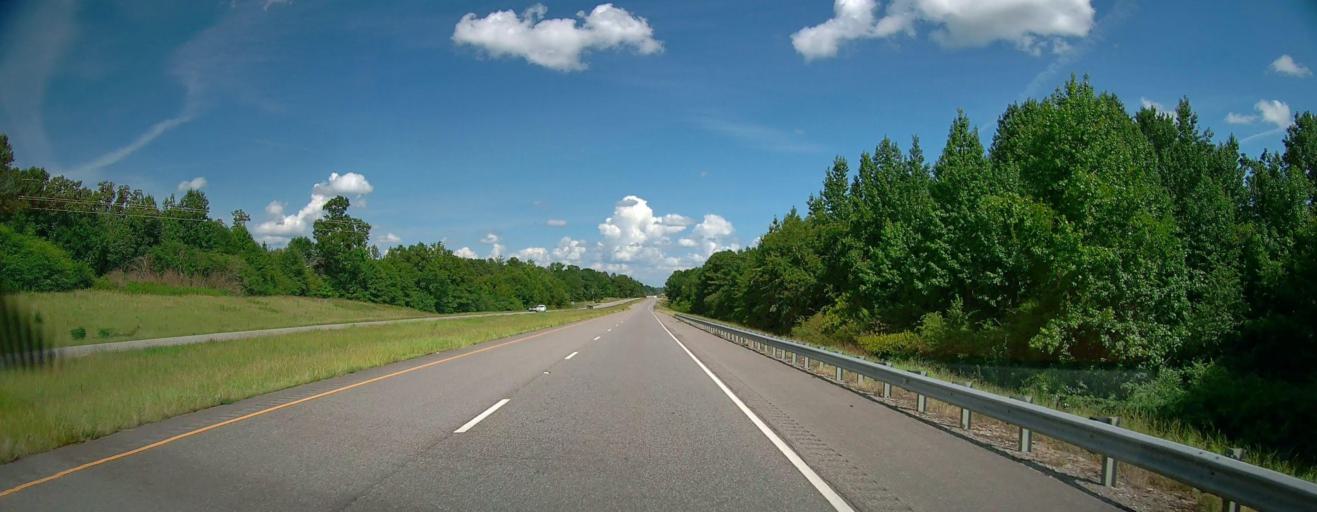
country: US
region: Alabama
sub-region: Pickens County
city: Reform
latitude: 33.3886
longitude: -88.0370
